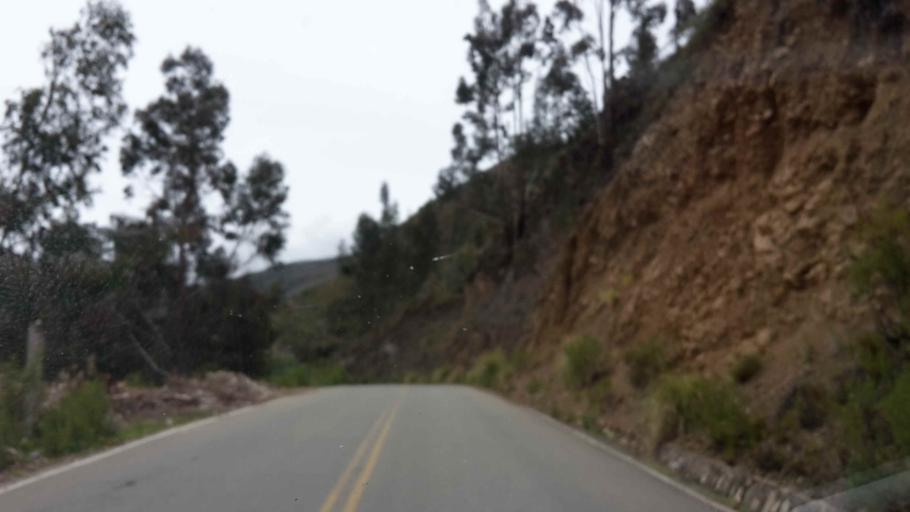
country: BO
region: Cochabamba
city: Colomi
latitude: -17.4016
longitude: -65.8112
